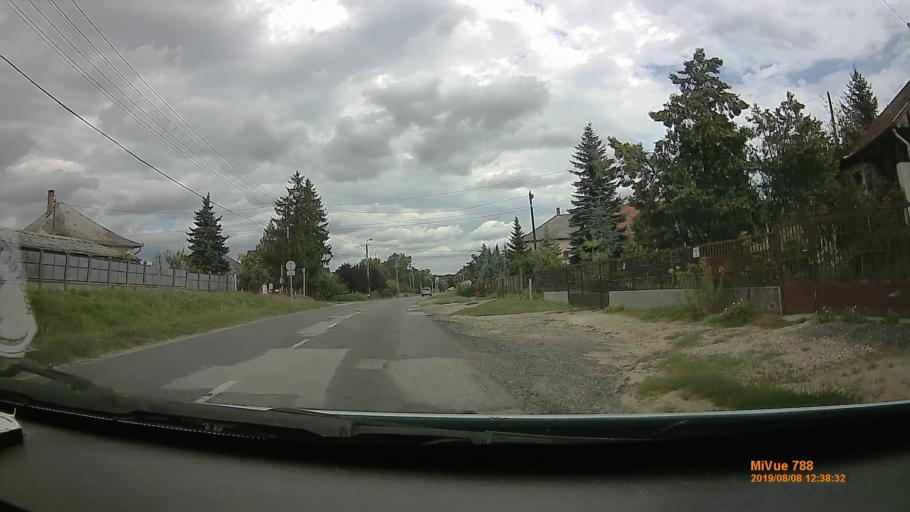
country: HU
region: Szabolcs-Szatmar-Bereg
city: Nyirbator
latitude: 47.8395
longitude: 22.1425
